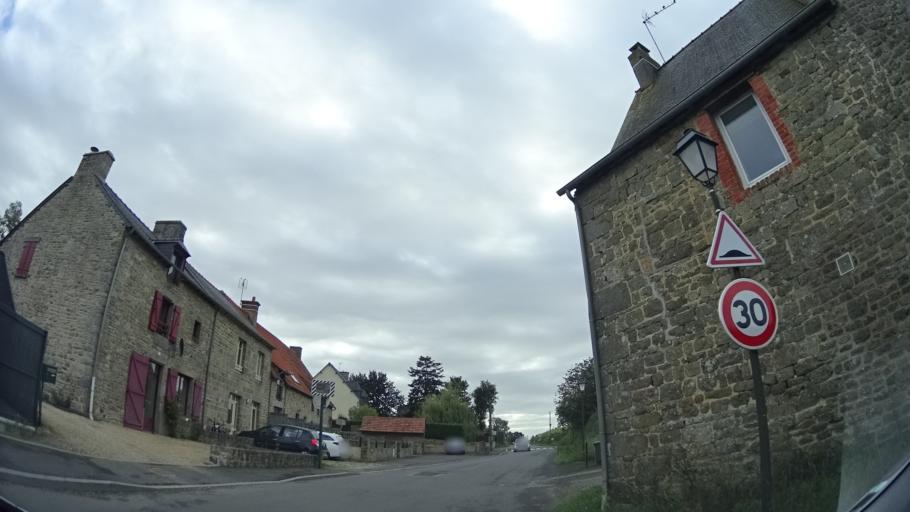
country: FR
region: Brittany
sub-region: Departement d'Ille-et-Vilaine
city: Dinge
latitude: 48.3575
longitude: -1.7116
